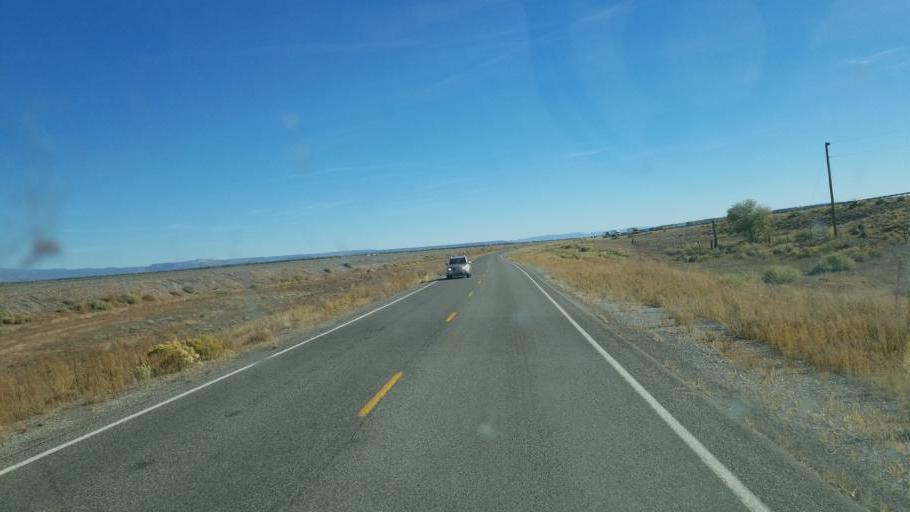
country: US
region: New Mexico
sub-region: Cibola County
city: Milan
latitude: 35.3469
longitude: -108.0102
